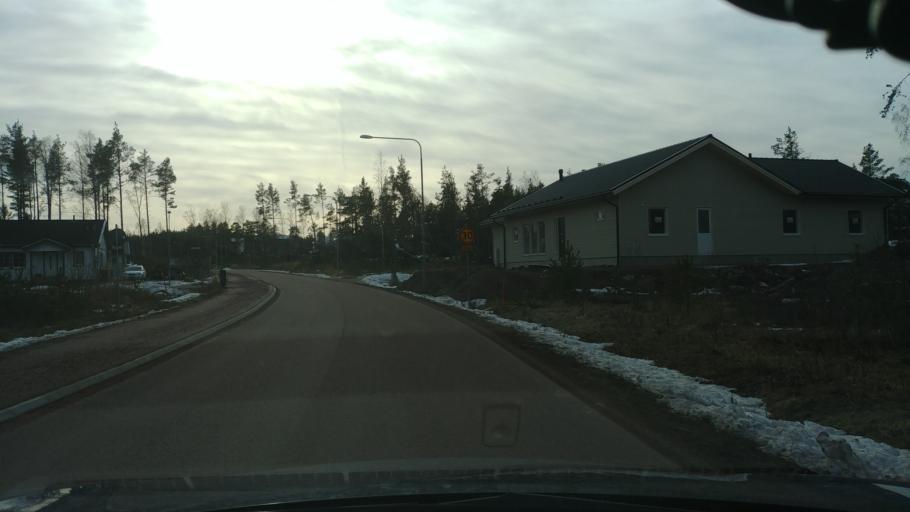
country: AX
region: Mariehamns stad
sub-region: Mariehamn
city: Mariehamn
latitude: 60.1019
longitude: 19.8928
